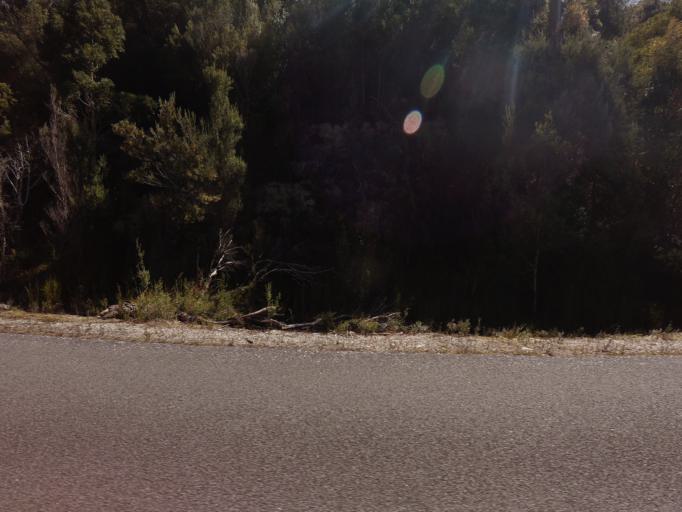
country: AU
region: Tasmania
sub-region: Huon Valley
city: Geeveston
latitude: -42.8580
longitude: 146.2306
